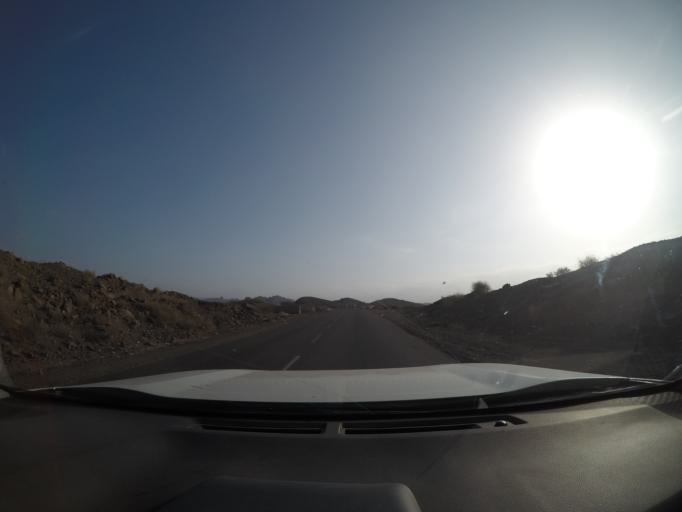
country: YE
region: Lahij
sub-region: Al Milah
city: Al Milah
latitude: 13.3844
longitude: 44.8109
